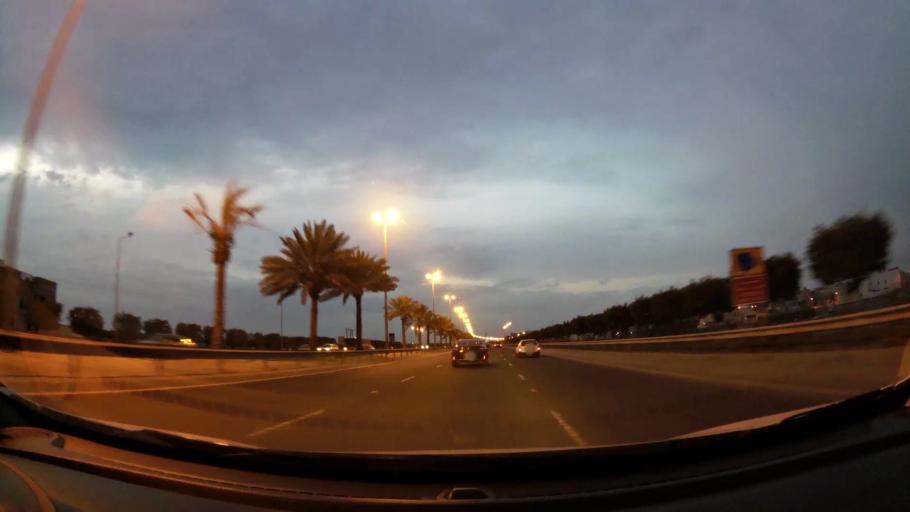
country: BH
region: Central Governorate
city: Madinat Hamad
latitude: 26.1509
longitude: 50.5083
